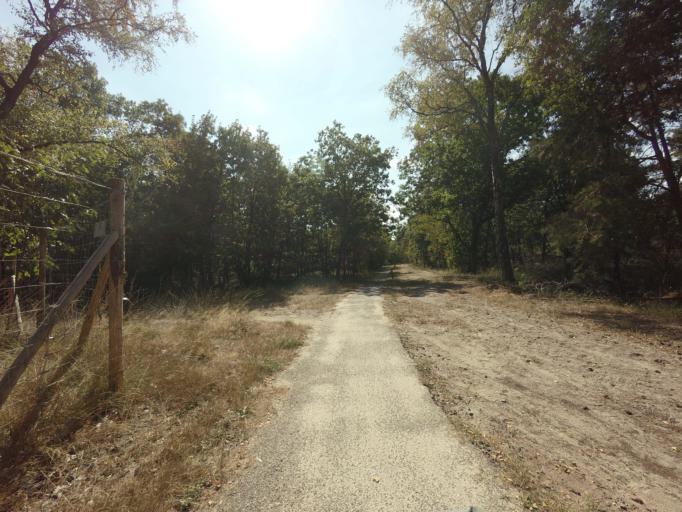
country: NL
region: North Brabant
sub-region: Gemeente Someren
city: Someren
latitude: 51.3652
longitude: 5.6579
